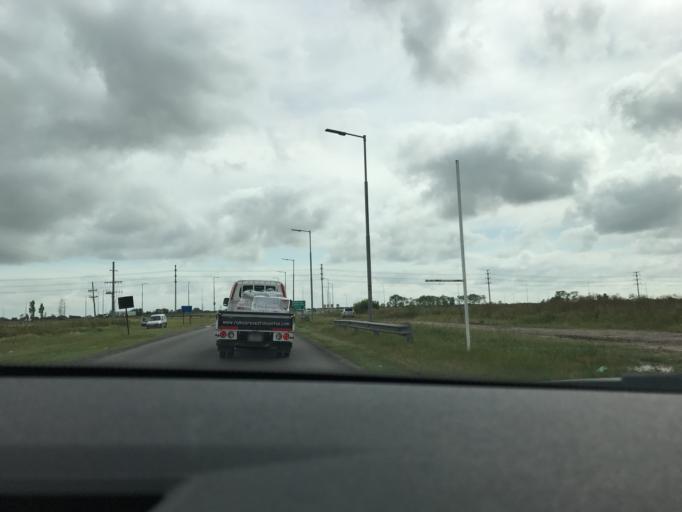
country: AR
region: Buenos Aires
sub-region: Partido de La Plata
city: La Plata
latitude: -34.8416
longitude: -58.0726
